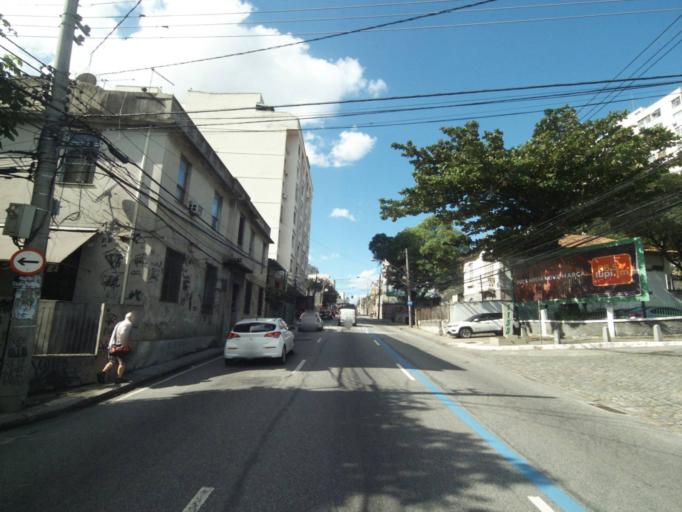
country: BR
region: Rio de Janeiro
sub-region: Rio De Janeiro
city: Rio de Janeiro
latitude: -22.9030
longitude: -43.2512
